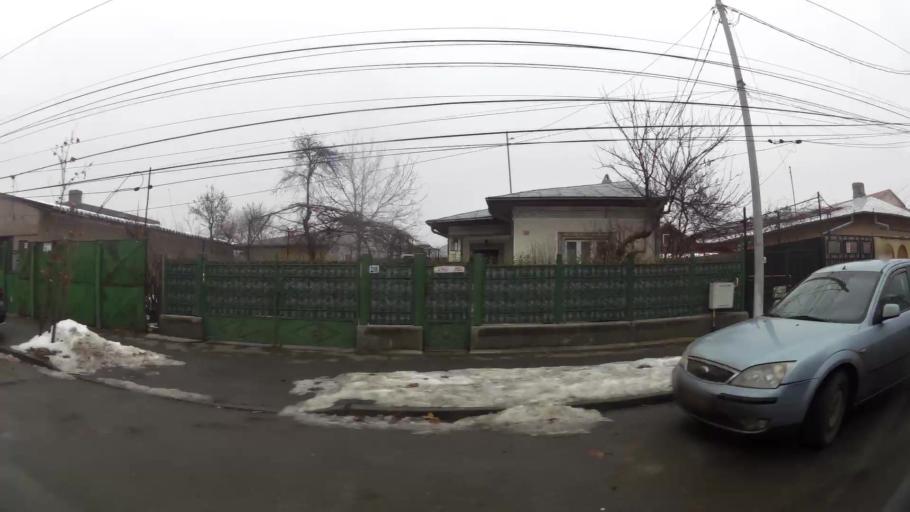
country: RO
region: Ilfov
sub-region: Comuna Chiajna
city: Rosu
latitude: 44.4696
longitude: 26.0200
